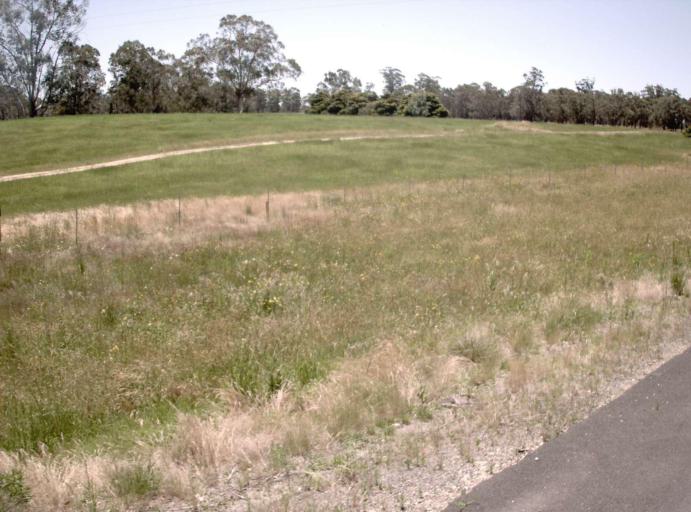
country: AU
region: Victoria
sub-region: East Gippsland
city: Lakes Entrance
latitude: -37.7558
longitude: 148.2767
